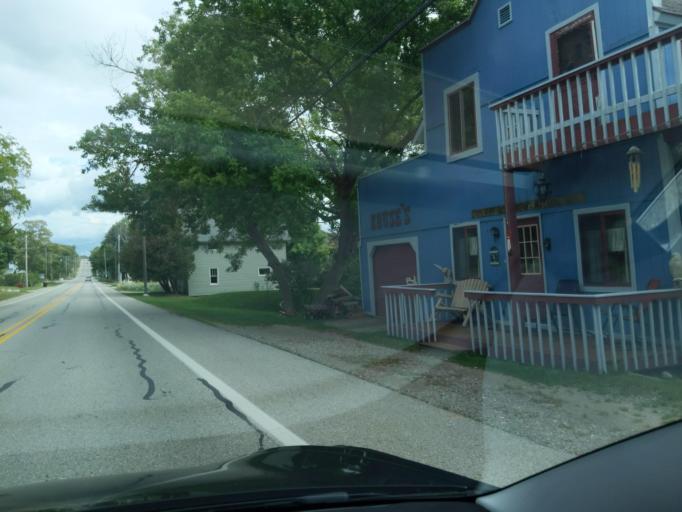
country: US
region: Michigan
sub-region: Antrim County
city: Bellaire
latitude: 45.1071
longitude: -85.3486
